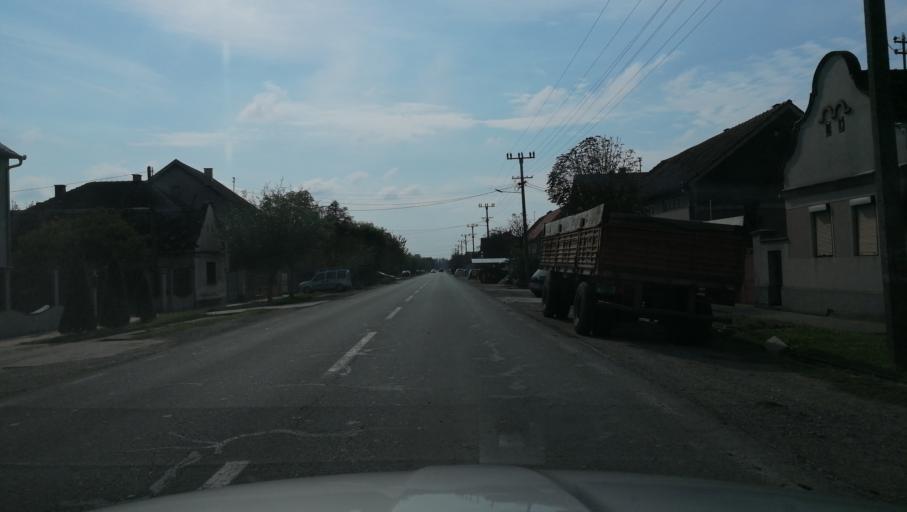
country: RS
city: Ravnje
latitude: 45.0207
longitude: 19.4020
